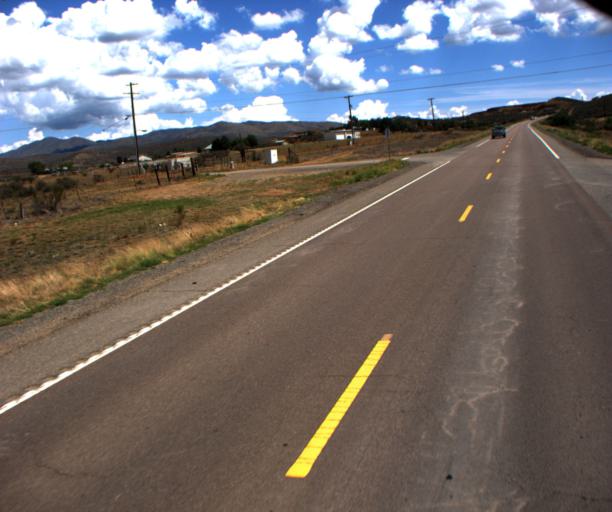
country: US
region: Arizona
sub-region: Yavapai County
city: Dewey-Humboldt
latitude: 34.5355
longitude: -112.2120
